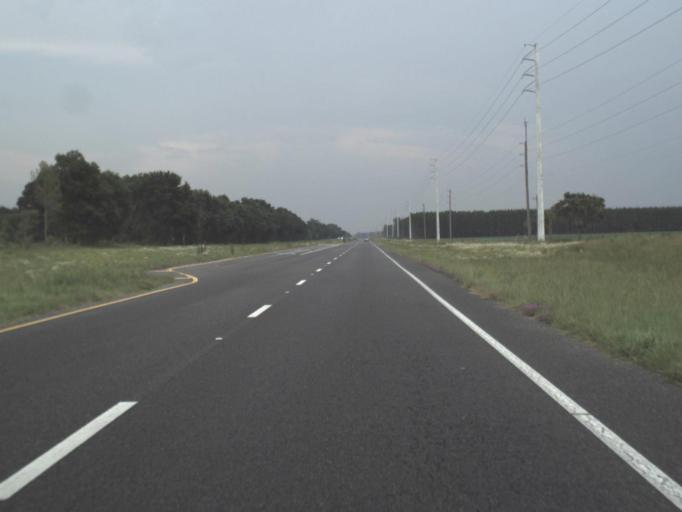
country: US
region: Florida
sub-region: Levy County
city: Chiefland
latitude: 29.4748
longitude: -82.7751
